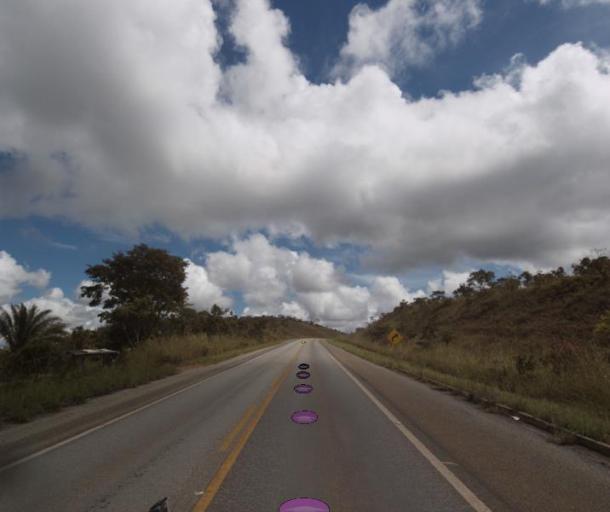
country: BR
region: Goias
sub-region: Pirenopolis
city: Pirenopolis
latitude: -15.7722
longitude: -48.5528
